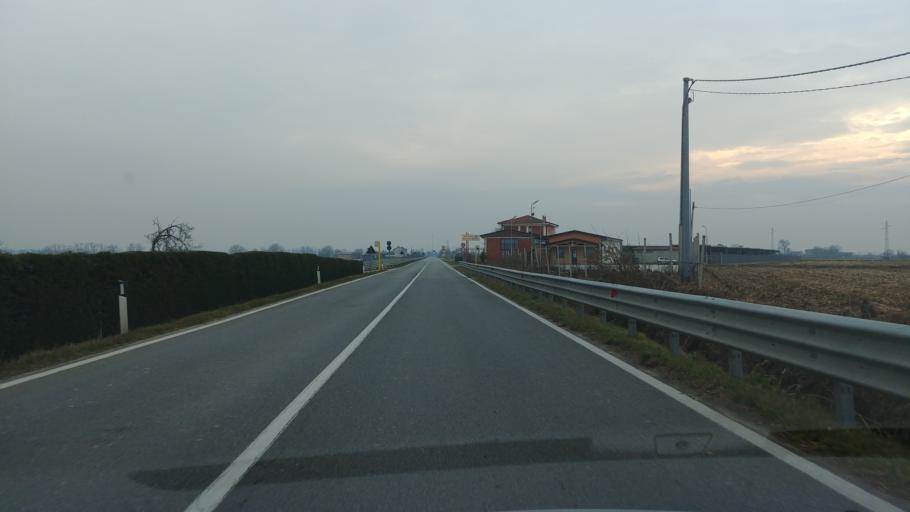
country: IT
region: Piedmont
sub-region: Provincia di Cuneo
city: Castelletto Stura
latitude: 44.4674
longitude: 7.6347
